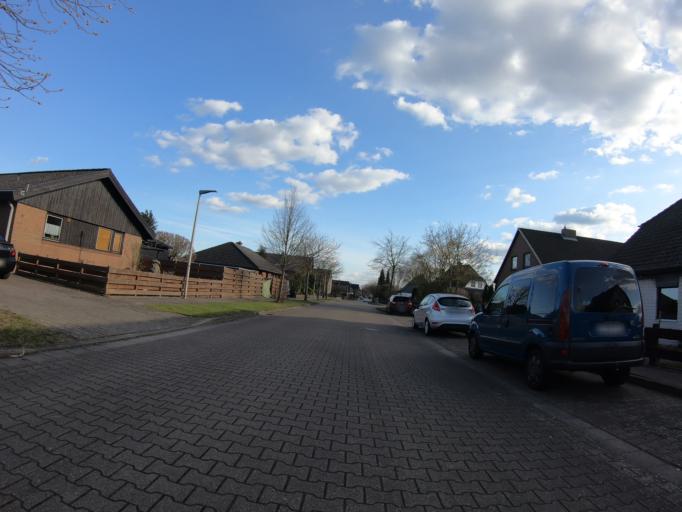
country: DE
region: Lower Saxony
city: Wesendorf
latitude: 52.5911
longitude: 10.5423
